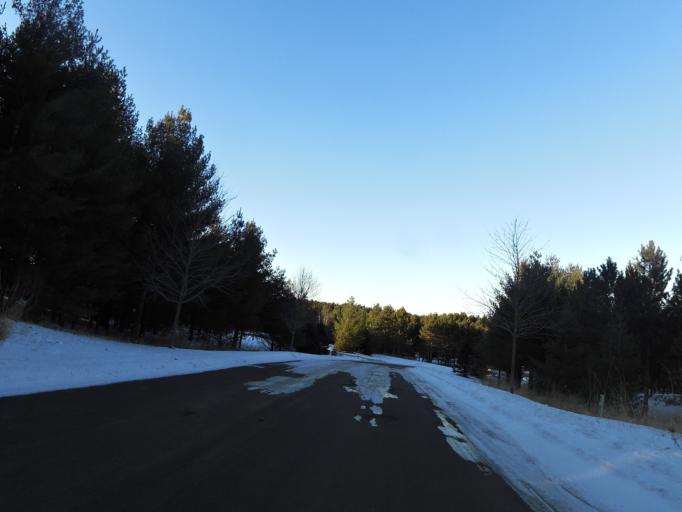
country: US
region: Minnesota
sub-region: Washington County
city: Lake Elmo
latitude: 44.9818
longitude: -92.8394
